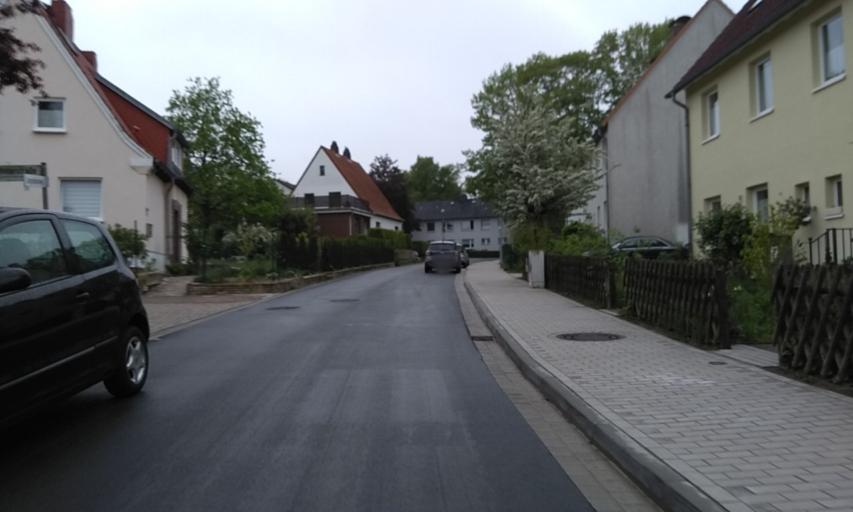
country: DE
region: Lower Saxony
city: Buxtehude
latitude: 53.4690
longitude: 9.6759
